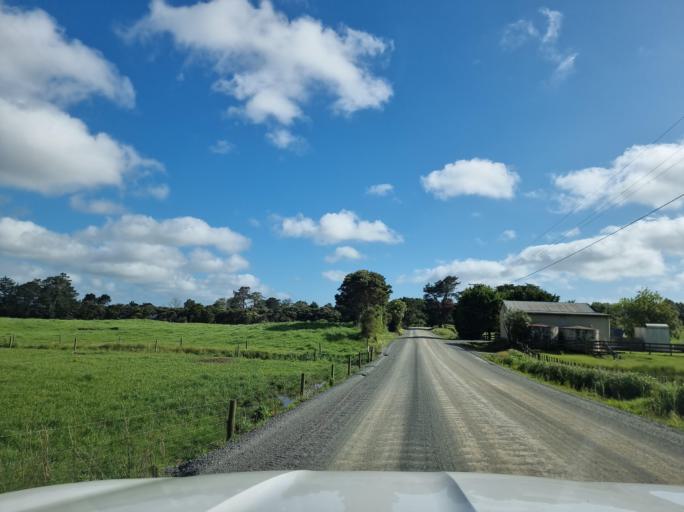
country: NZ
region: Auckland
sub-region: Auckland
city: Wellsford
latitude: -36.1289
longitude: 174.5934
